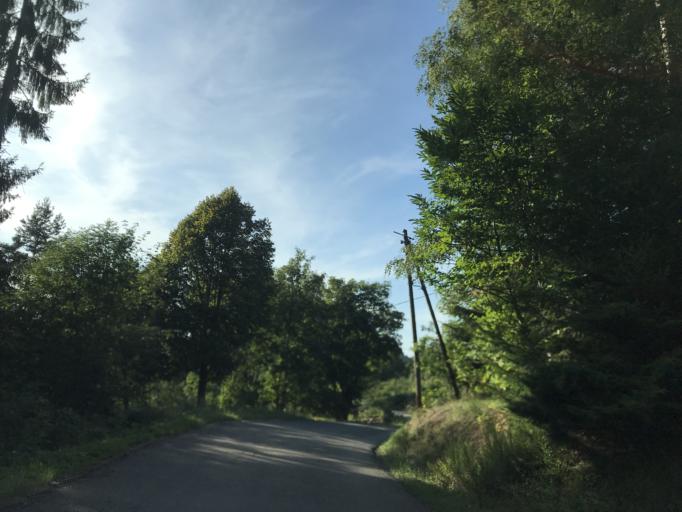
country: FR
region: Auvergne
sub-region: Departement du Puy-de-Dome
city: Job
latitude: 45.6752
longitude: 3.7346
